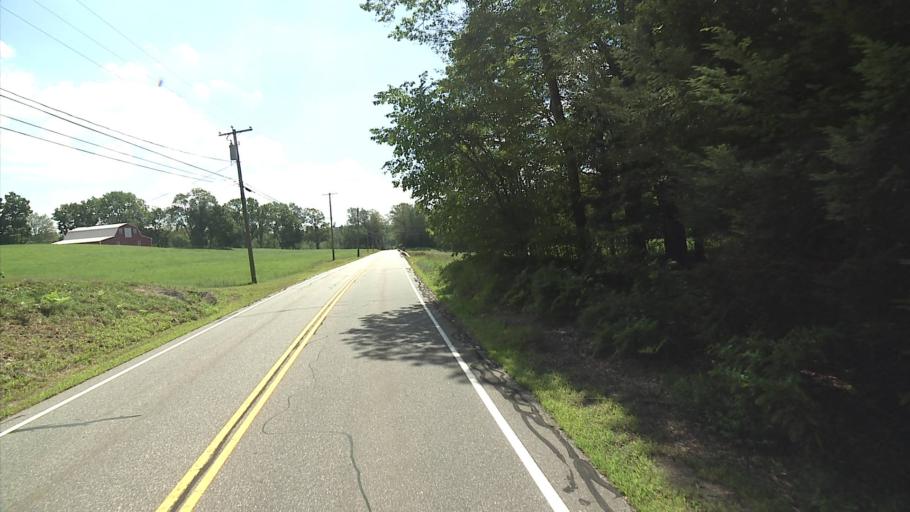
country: US
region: Connecticut
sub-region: Windham County
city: South Woodstock
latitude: 41.9216
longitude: -72.0800
